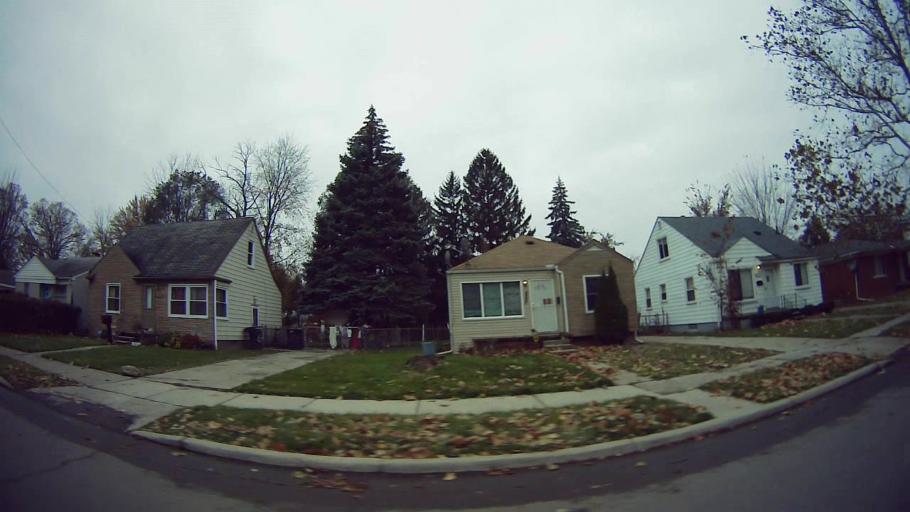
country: US
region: Michigan
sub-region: Wayne County
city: Dearborn Heights
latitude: 42.3371
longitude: -83.2352
